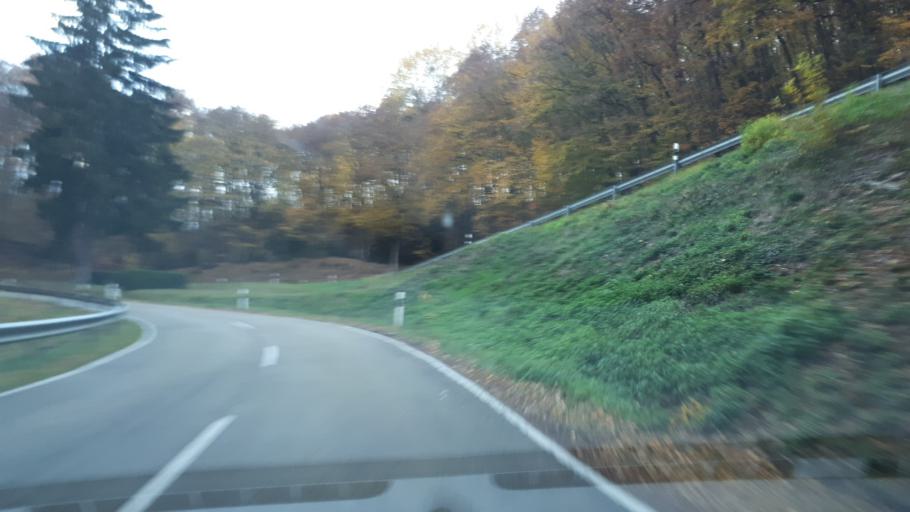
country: DE
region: Rheinland-Pfalz
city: Bad Bertrich
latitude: 50.0789
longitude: 7.0187
